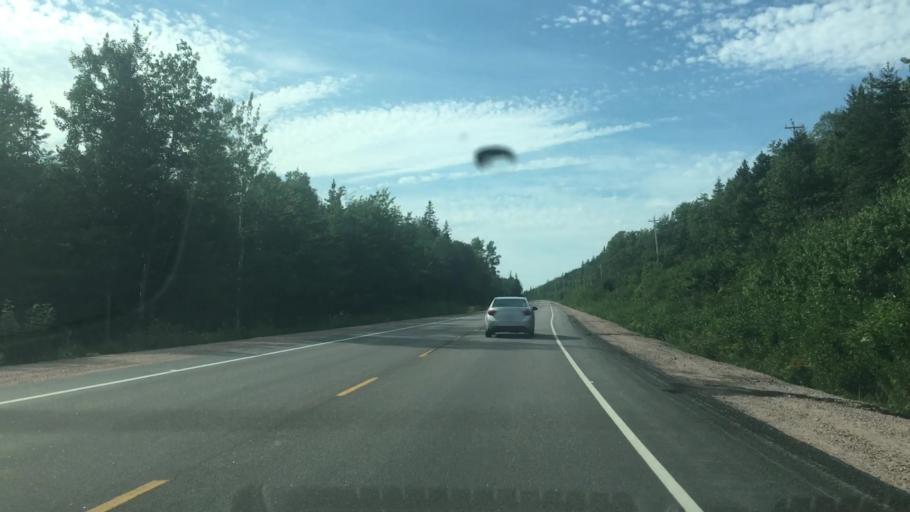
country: CA
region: Nova Scotia
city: Sydney Mines
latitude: 46.8154
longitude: -60.3418
